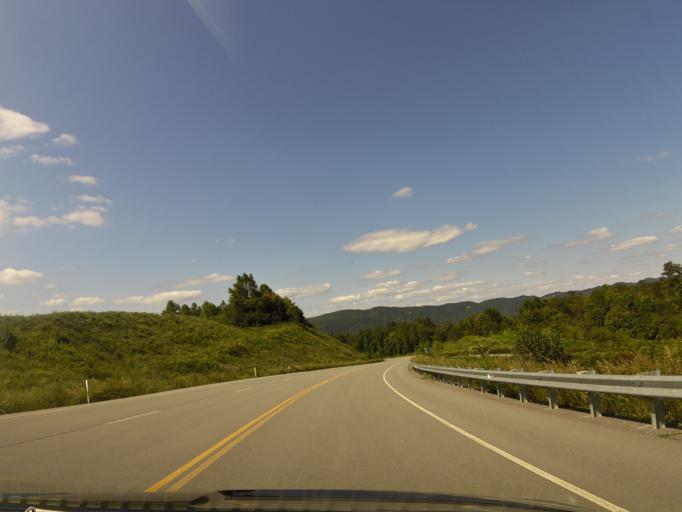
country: US
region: Kentucky
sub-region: Bell County
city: Pineville
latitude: 36.7329
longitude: -83.5898
